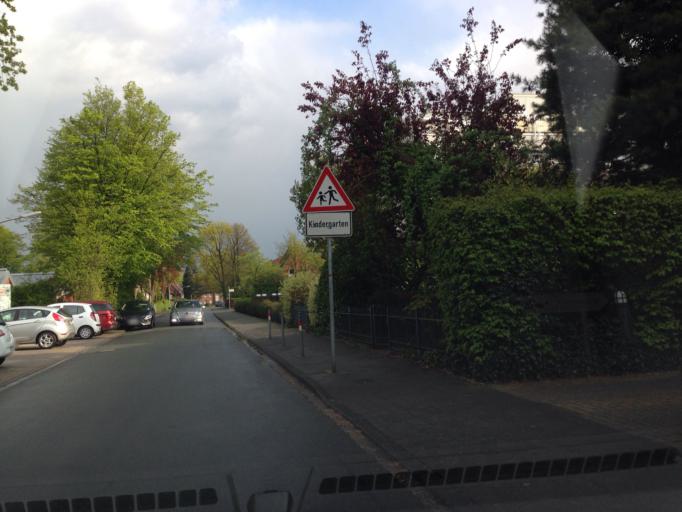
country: DE
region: North Rhine-Westphalia
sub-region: Regierungsbezirk Munster
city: Muenster
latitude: 51.9979
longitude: 7.5590
